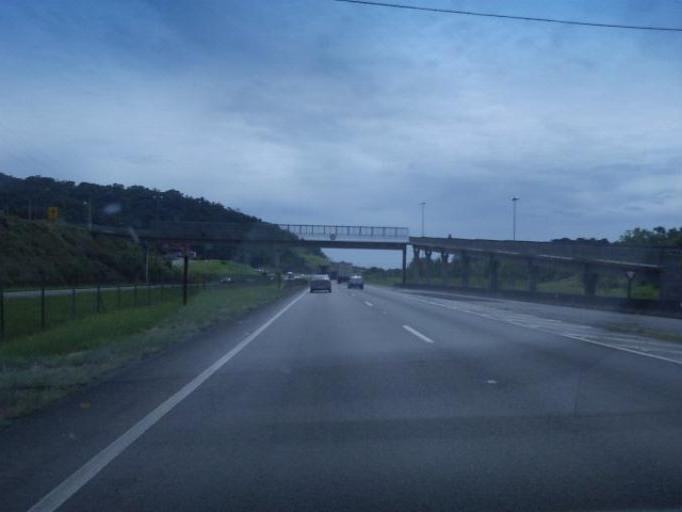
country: BR
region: Sao Paulo
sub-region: Miracatu
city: Miracatu
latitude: -24.2897
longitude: -47.4633
